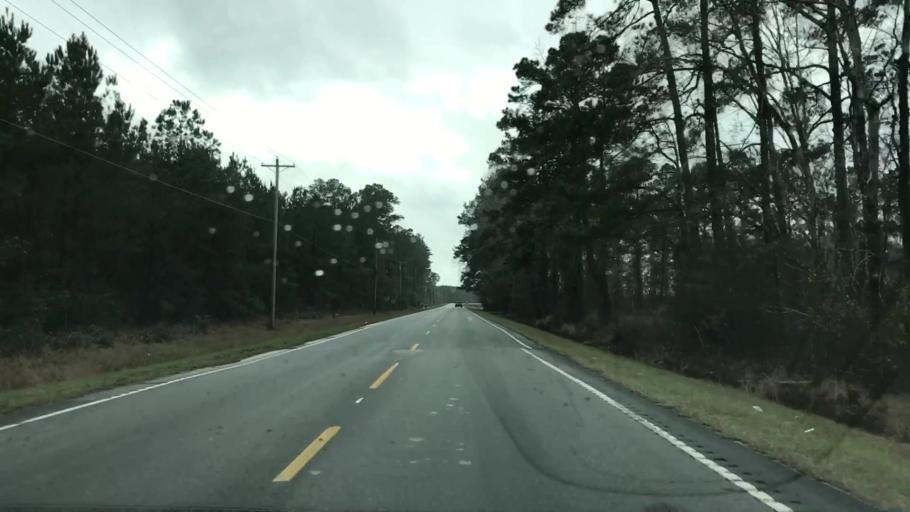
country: US
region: South Carolina
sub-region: Horry County
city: Socastee
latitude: 33.7306
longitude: -79.0835
